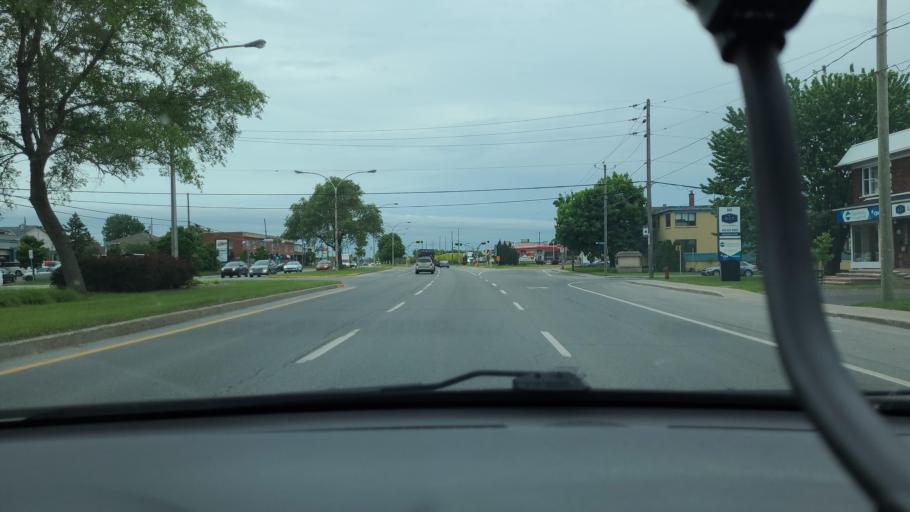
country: CA
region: Quebec
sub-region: Monteregie
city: La Prairie
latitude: 45.4092
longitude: -73.4957
